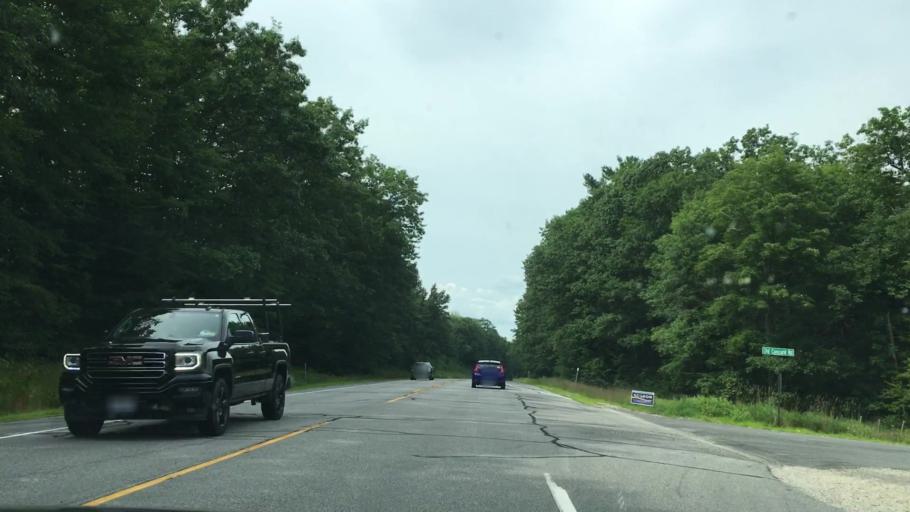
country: US
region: New Hampshire
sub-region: Hillsborough County
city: Antrim
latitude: 43.0710
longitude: -71.9164
